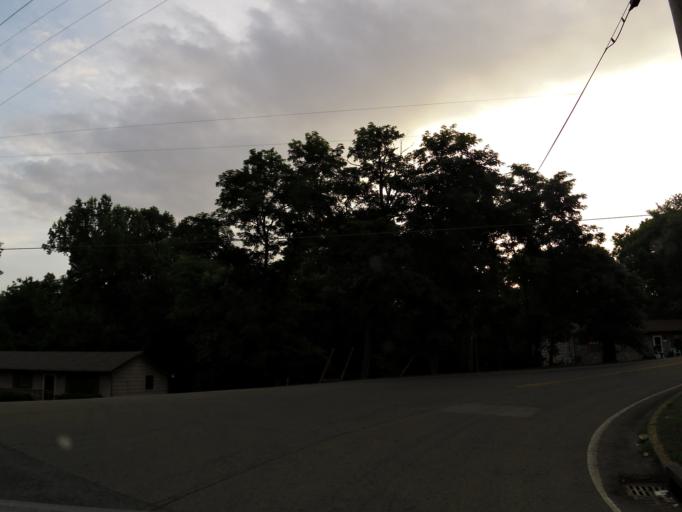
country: US
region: Tennessee
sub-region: Knox County
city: Knoxville
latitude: 35.9779
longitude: -83.8863
